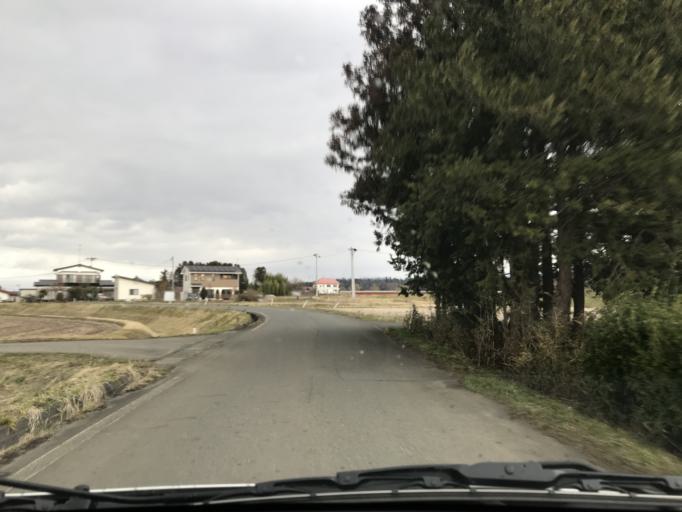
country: JP
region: Iwate
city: Mizusawa
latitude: 39.0911
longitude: 141.1792
